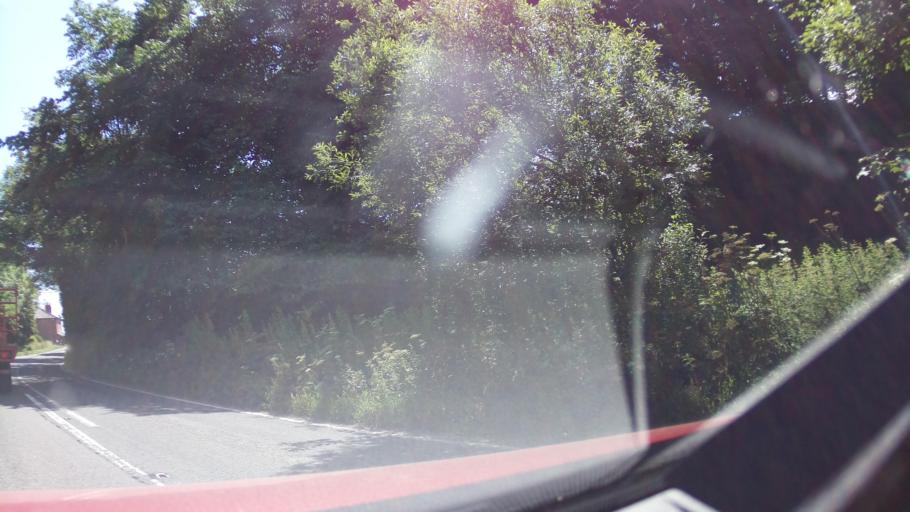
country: GB
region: England
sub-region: Derbyshire
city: Ashbourne
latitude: 53.0847
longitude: -1.7622
